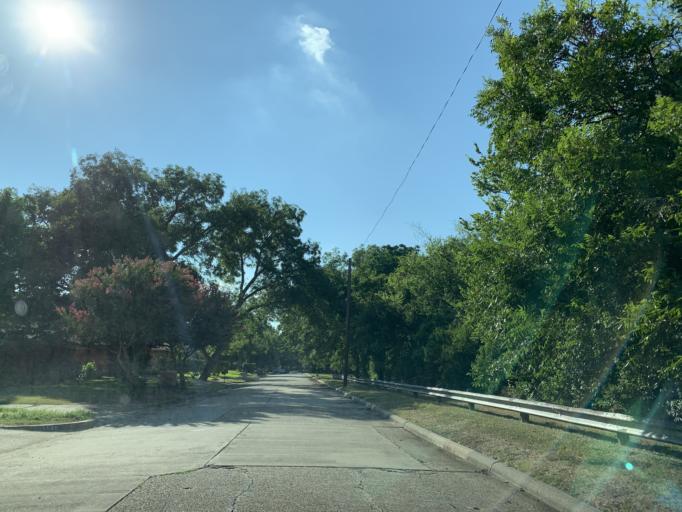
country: US
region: Texas
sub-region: Dallas County
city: Cockrell Hill
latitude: 32.6838
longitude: -96.8065
